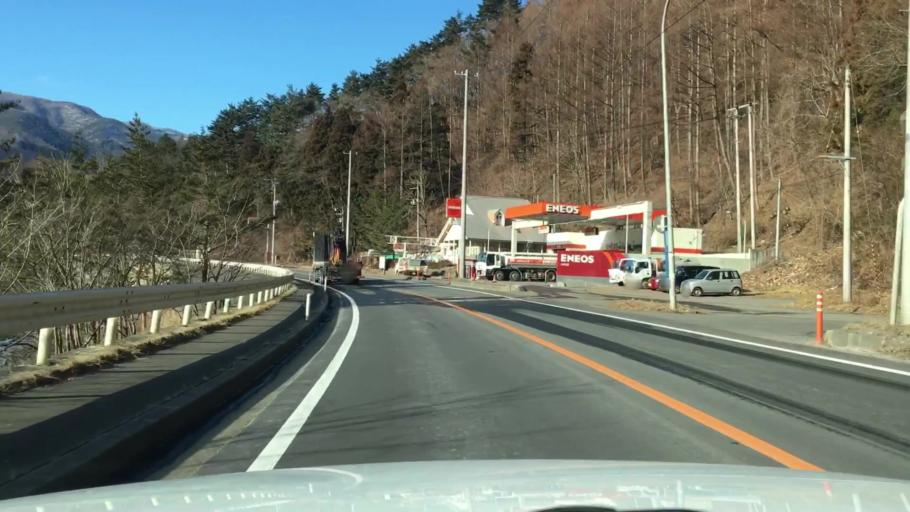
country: JP
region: Iwate
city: Tono
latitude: 39.6402
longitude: 141.6002
